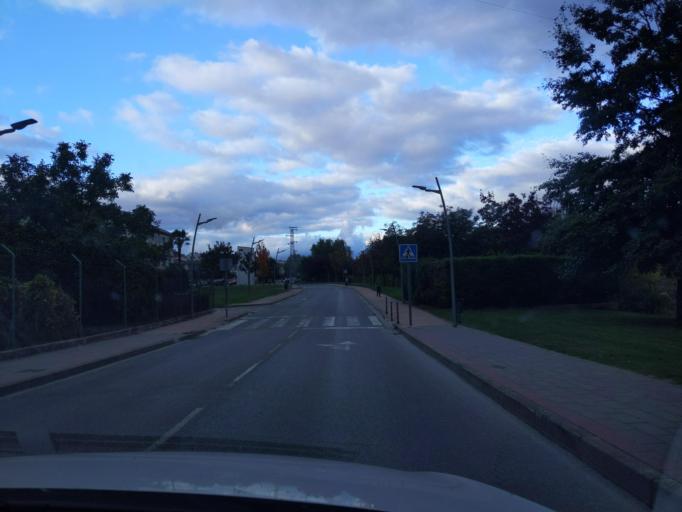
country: ES
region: La Rioja
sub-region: Provincia de La Rioja
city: Najera
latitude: 42.4133
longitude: -2.7341
